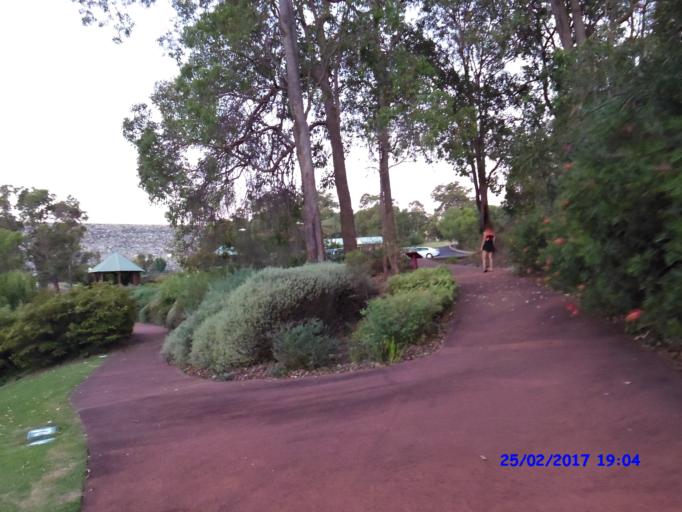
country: AU
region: Western Australia
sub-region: Harvey
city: Harvey
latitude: -33.0795
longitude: 115.9283
